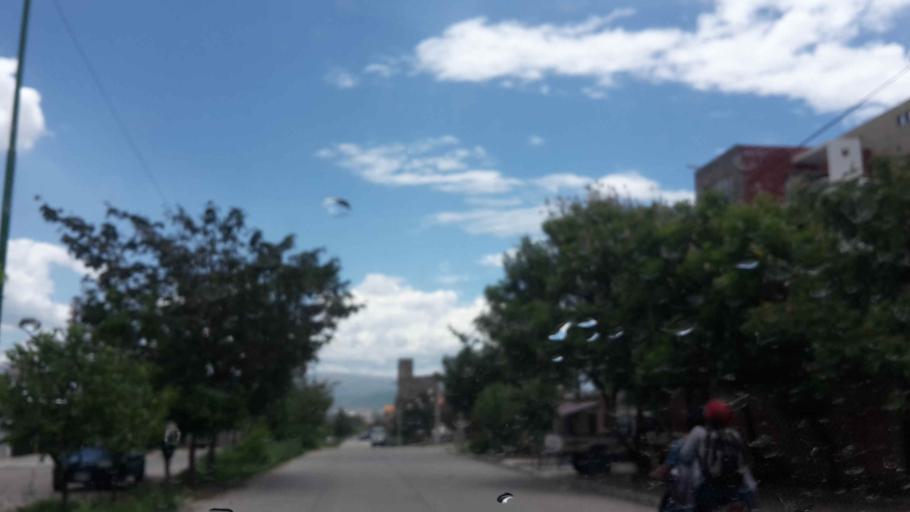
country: BO
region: Cochabamba
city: Cochabamba
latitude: -17.3542
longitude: -66.1833
